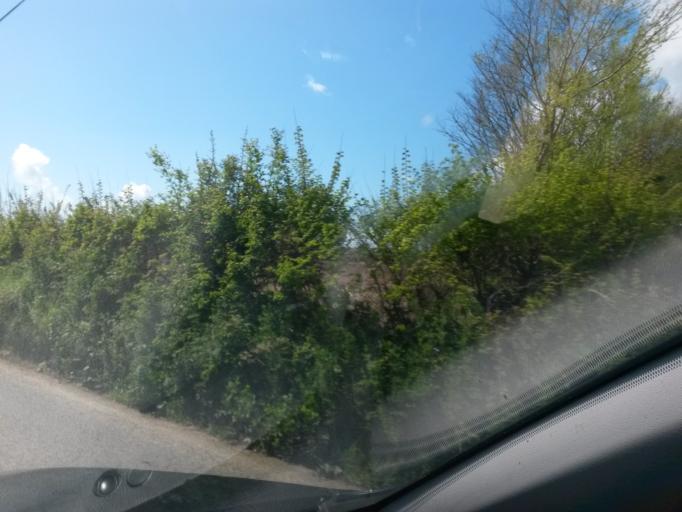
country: IE
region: Munster
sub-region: Waterford
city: Dunmore East
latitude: 52.2432
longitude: -6.8595
